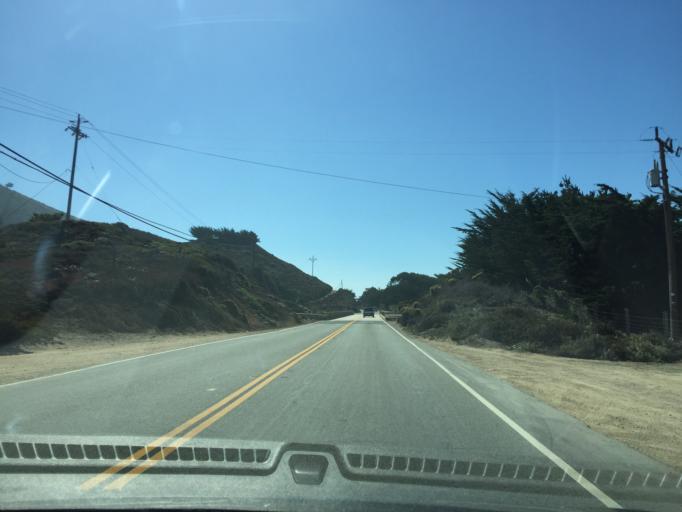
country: US
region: California
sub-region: Monterey County
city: Carmel-by-the-Sea
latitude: 36.4183
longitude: -121.9135
